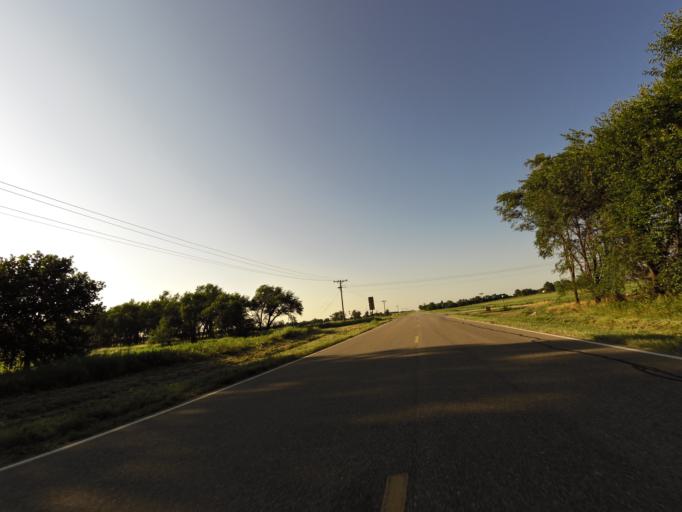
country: US
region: Kansas
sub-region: Reno County
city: Buhler
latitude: 38.1730
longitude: -97.8486
